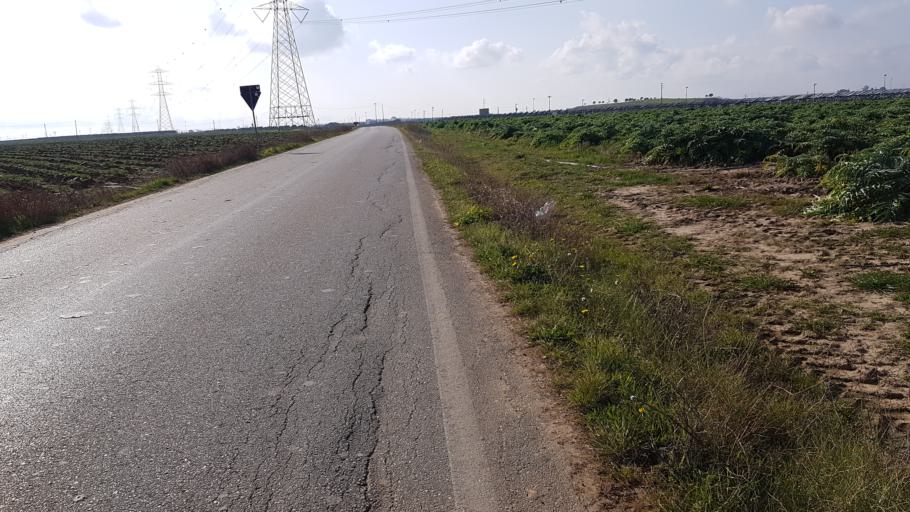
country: IT
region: Apulia
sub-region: Provincia di Brindisi
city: La Rosa
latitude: 40.5928
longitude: 17.9036
